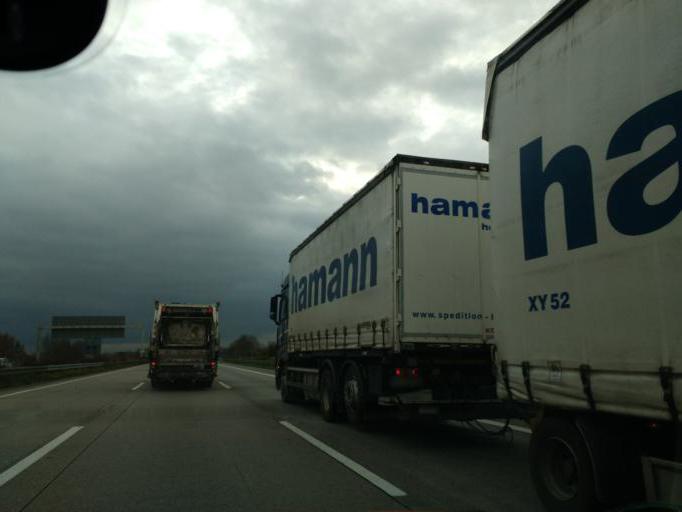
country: DE
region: Lower Saxony
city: Lehrte
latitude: 52.3854
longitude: 9.8989
